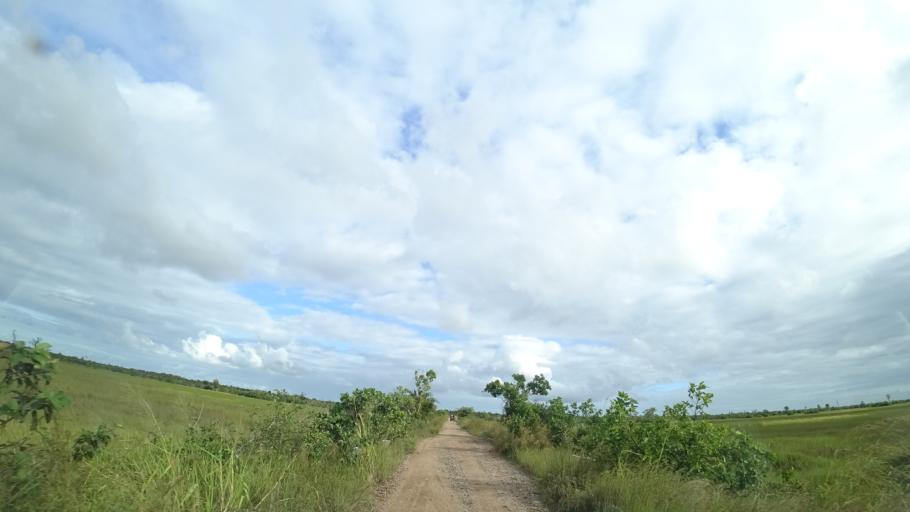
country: MZ
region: Sofala
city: Beira
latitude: -19.6266
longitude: 35.0603
